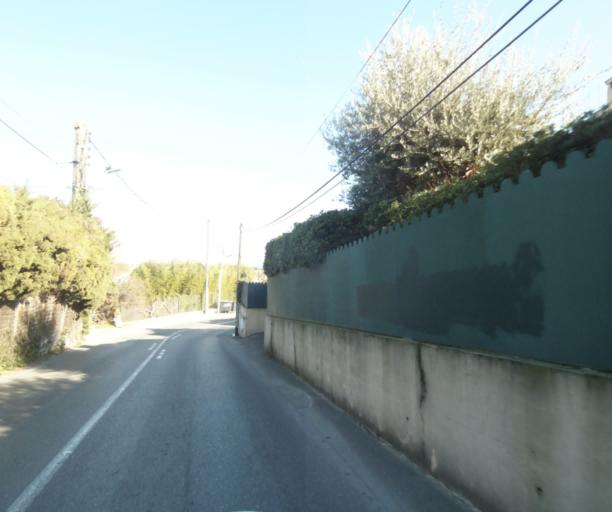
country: FR
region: Provence-Alpes-Cote d'Azur
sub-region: Departement des Alpes-Maritimes
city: Biot
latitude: 43.6041
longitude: 7.1073
